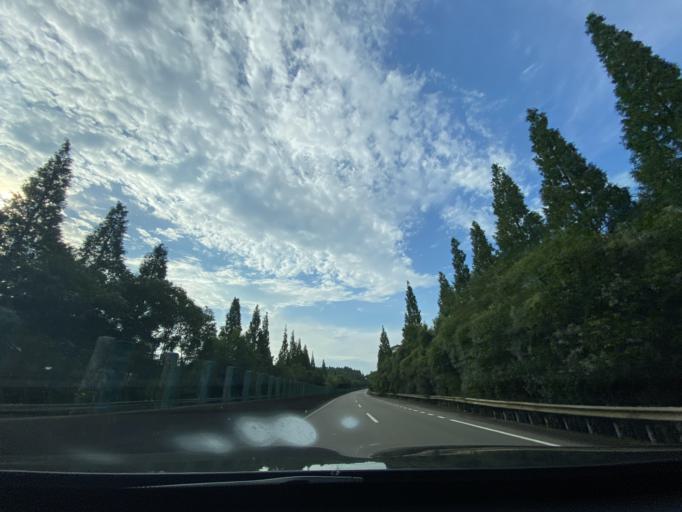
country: CN
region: Sichuan
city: Jiancheng
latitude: 30.2629
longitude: 104.6064
